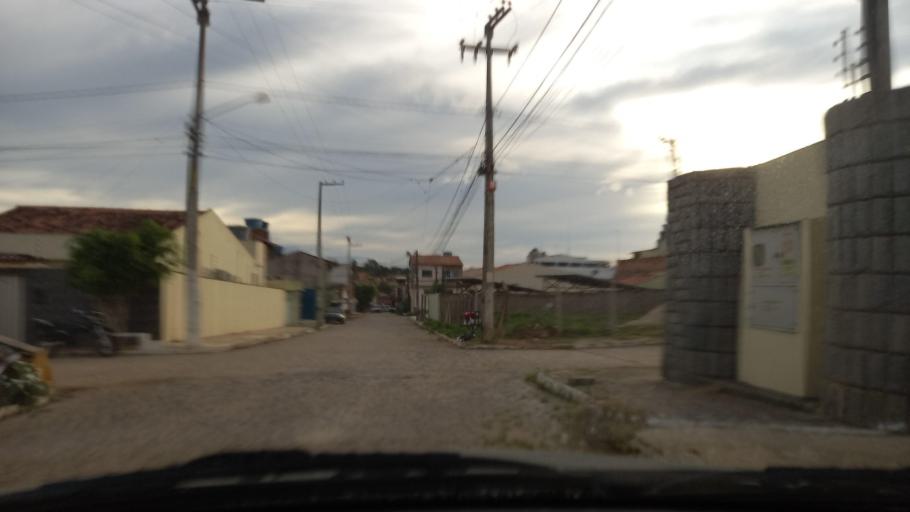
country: BR
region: Pernambuco
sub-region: Gravata
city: Gravata
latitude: -8.1951
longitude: -35.5747
